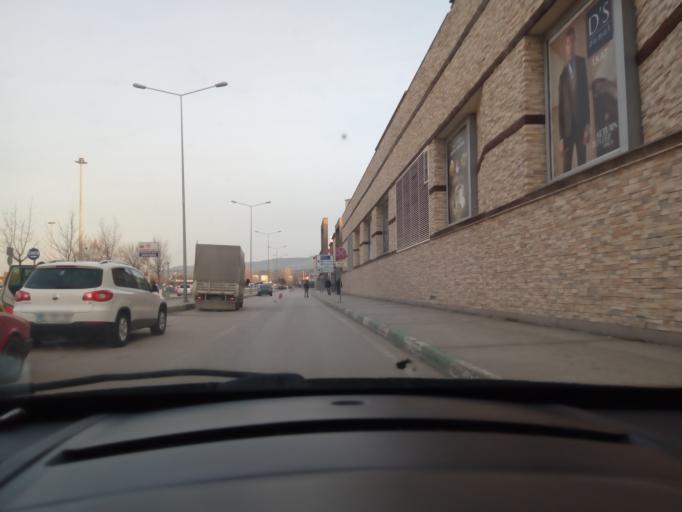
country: TR
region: Bursa
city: Demirtas
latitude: 40.2659
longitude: 29.0540
